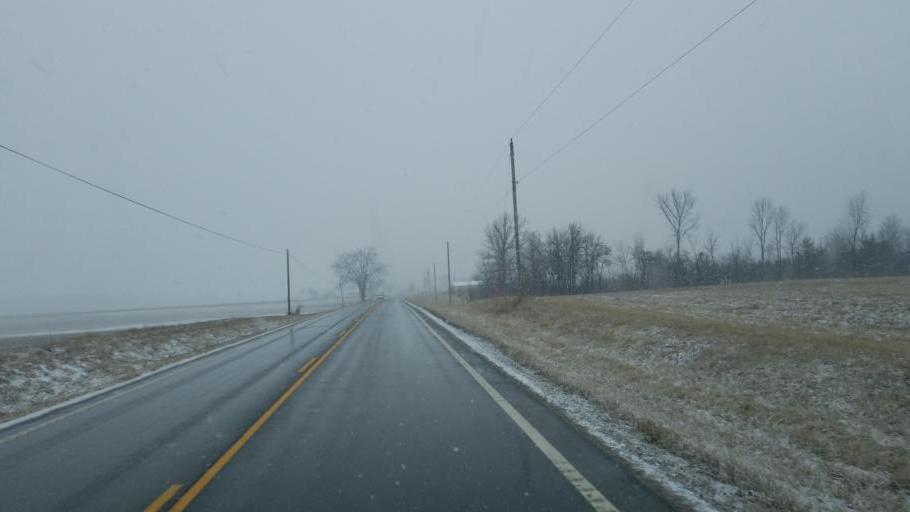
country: US
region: Ohio
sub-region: Defiance County
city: Hicksville
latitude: 41.3365
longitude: -84.7478
